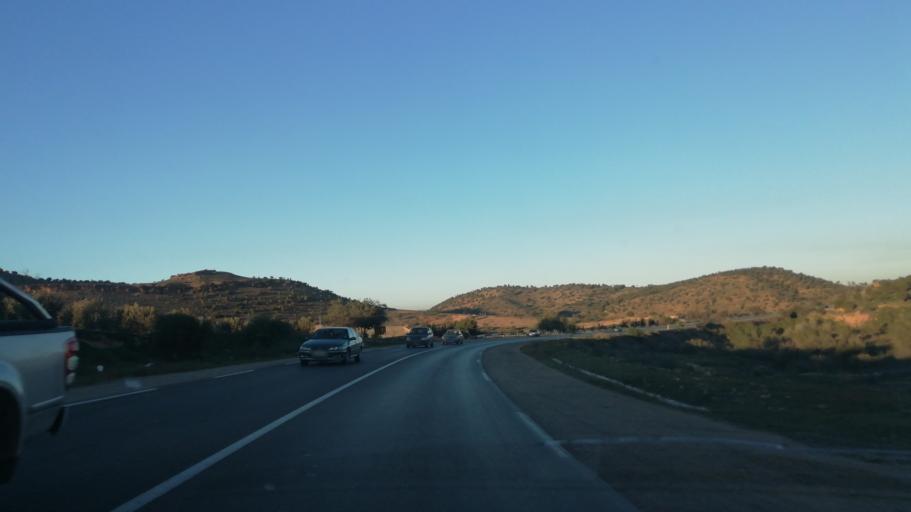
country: DZ
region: Tlemcen
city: Nedroma
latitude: 34.8637
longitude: -1.6785
